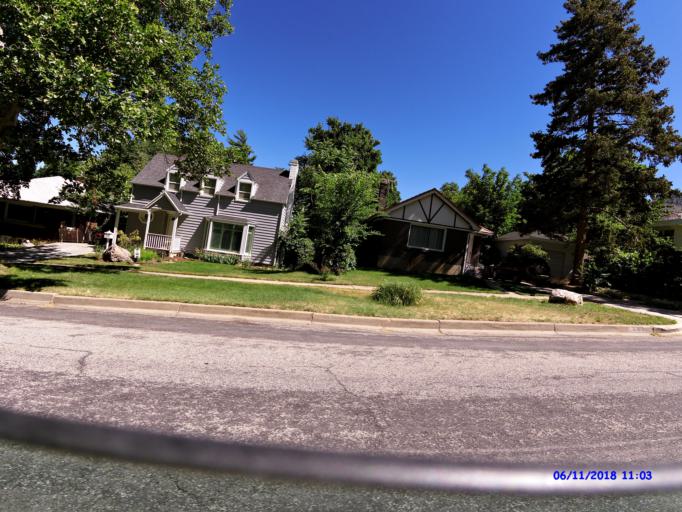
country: US
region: Utah
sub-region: Weber County
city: Ogden
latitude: 41.2181
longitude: -111.9382
